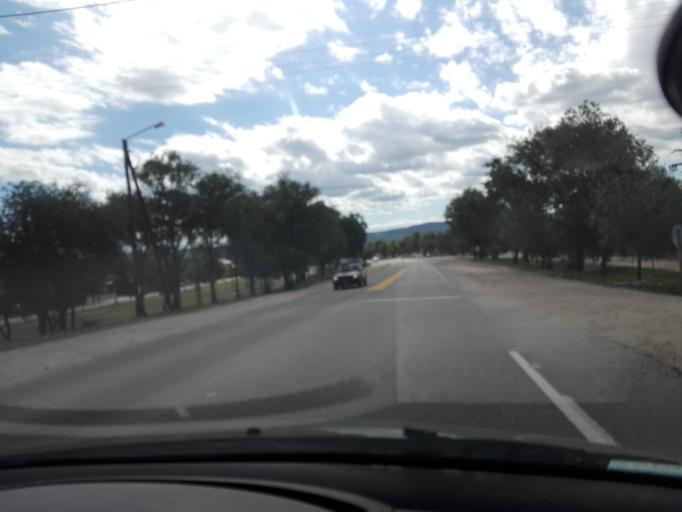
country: AR
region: Cordoba
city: Mina Clavero
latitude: -31.7419
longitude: -65.0002
